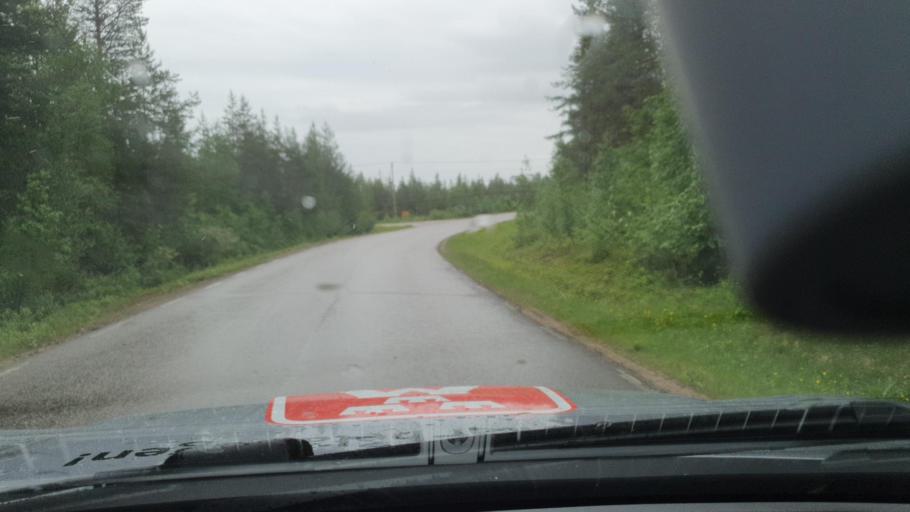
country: SE
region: Norrbotten
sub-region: Pajala Kommun
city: Pajala
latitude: 66.8305
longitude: 23.1180
